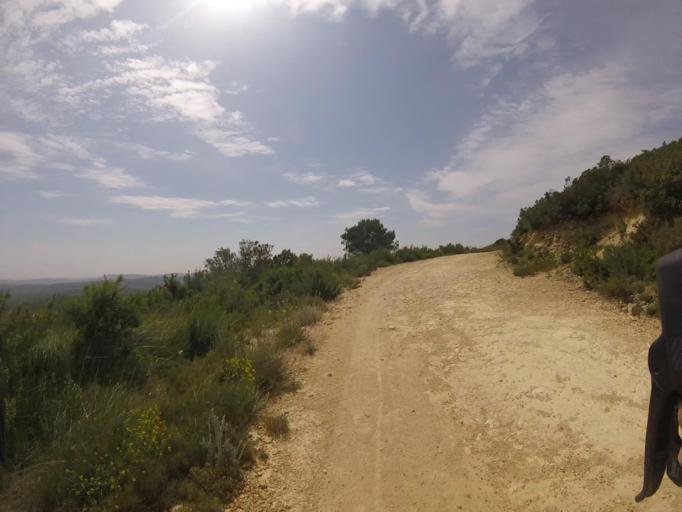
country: ES
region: Valencia
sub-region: Provincia de Castello
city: Cuevas de Vinroma
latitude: 40.2630
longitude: 0.1135
